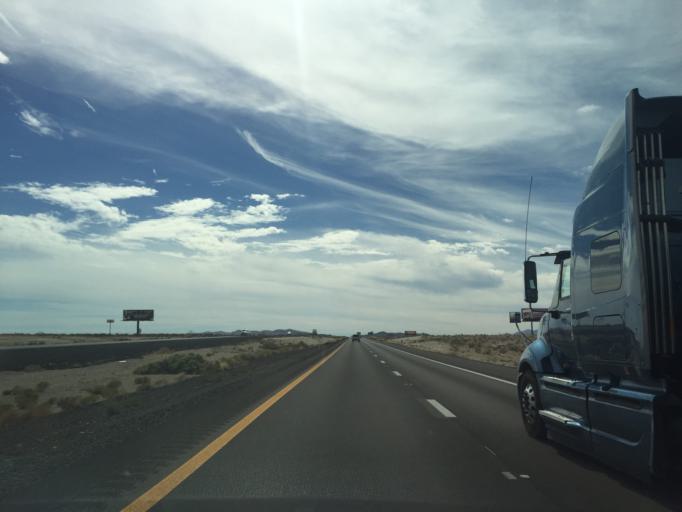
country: US
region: Nevada
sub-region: Clark County
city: Moapa Town
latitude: 36.5183
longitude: -114.7397
